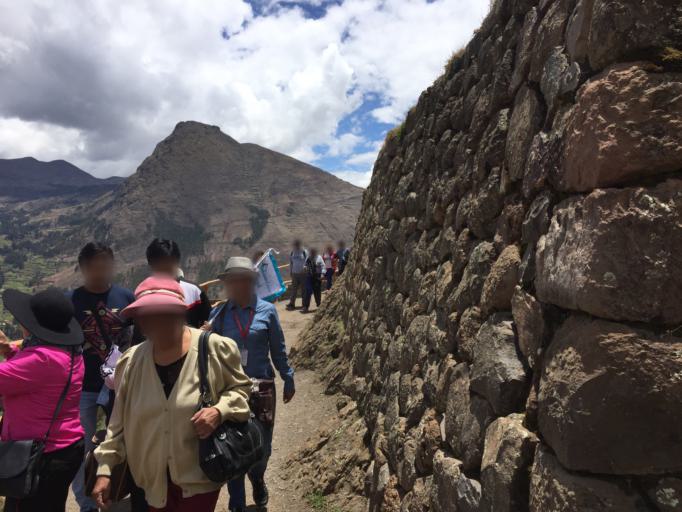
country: PE
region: Cusco
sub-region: Provincia de Calca
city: Pisac
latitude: -13.4065
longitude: -71.8415
